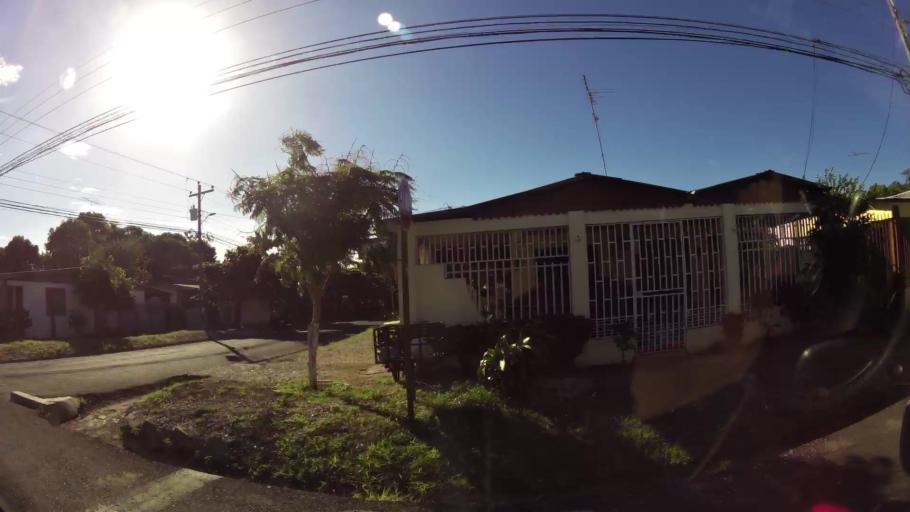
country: CR
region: Guanacaste
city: Belen
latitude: 10.4434
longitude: -85.5517
